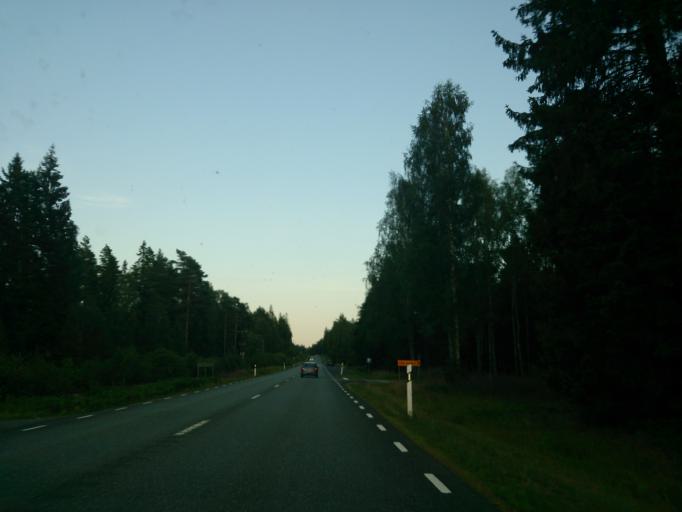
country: SE
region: Joenkoeping
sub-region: Varnamo Kommun
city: Bor
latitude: 57.0590
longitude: 14.1995
